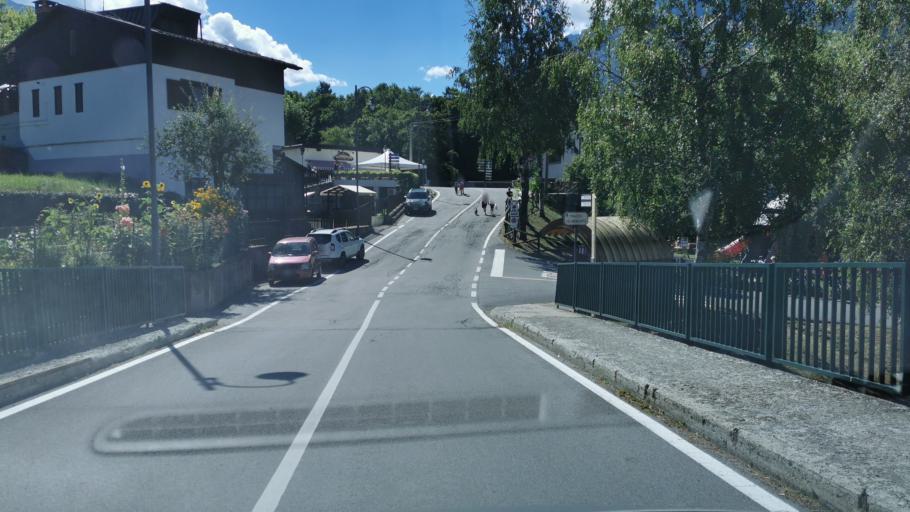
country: IT
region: Piedmont
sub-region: Provincia di Cuneo
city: Entracque
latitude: 44.2402
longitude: 7.3970
